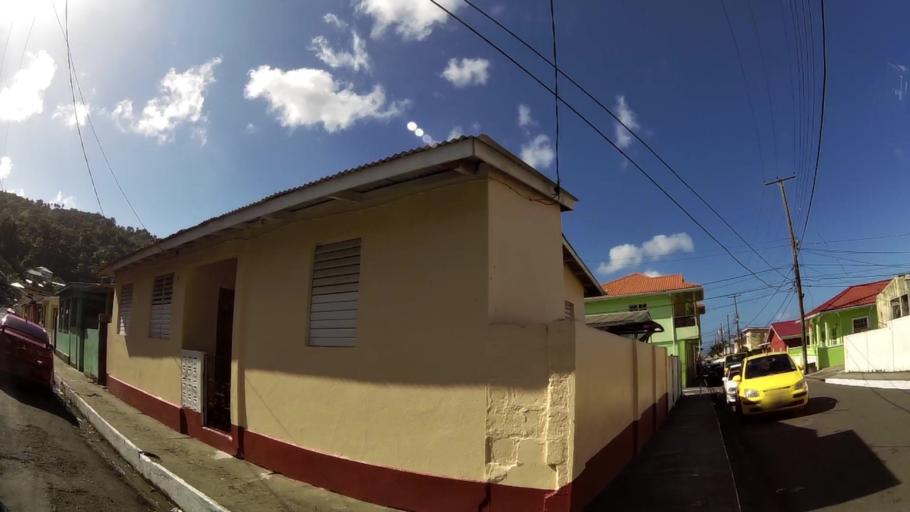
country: LC
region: Soufriere
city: Soufriere
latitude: 13.8554
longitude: -61.0582
